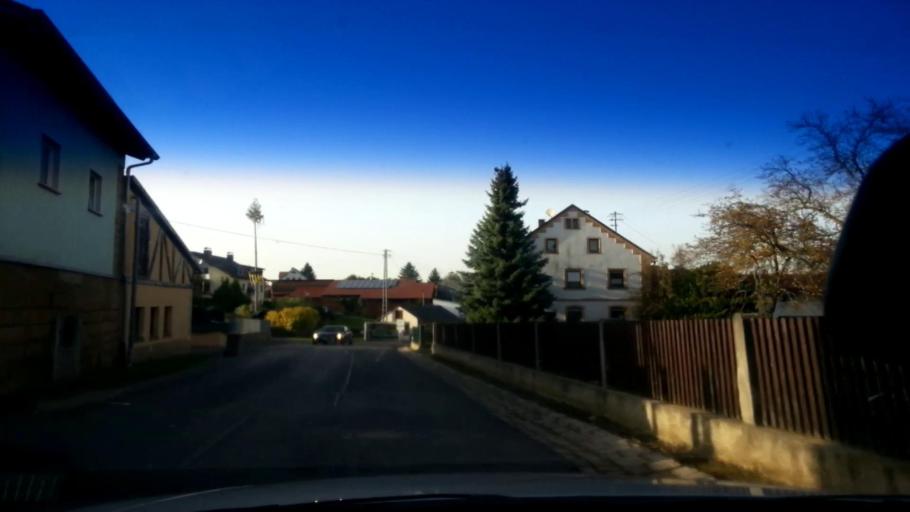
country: DE
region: Bavaria
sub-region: Upper Franconia
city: Schesslitz
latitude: 49.9600
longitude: 11.0576
